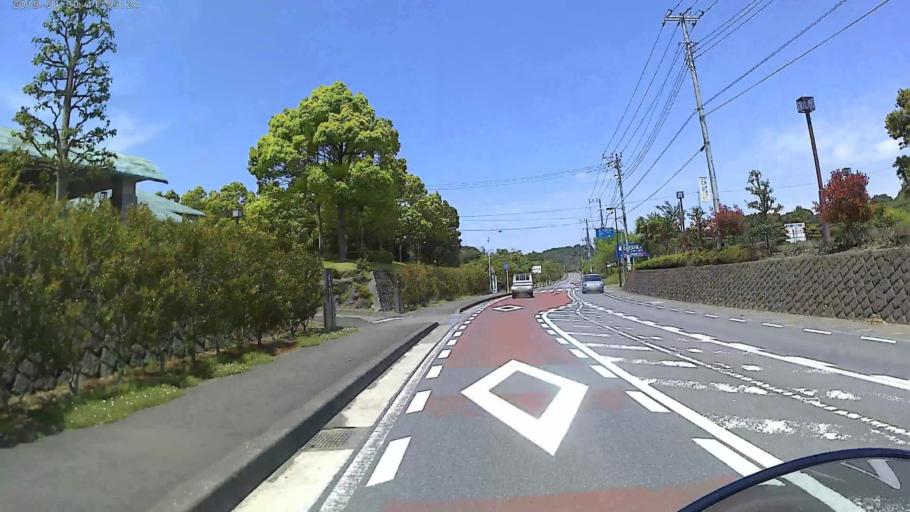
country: JP
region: Kanagawa
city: Zama
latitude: 35.5068
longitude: 139.3285
